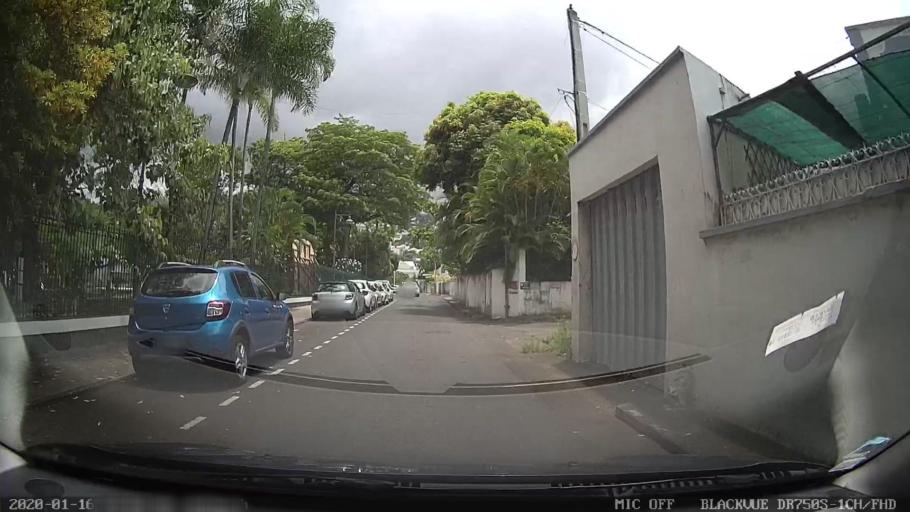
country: RE
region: Reunion
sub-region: Reunion
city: Saint-Denis
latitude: -20.8872
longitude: 55.4497
